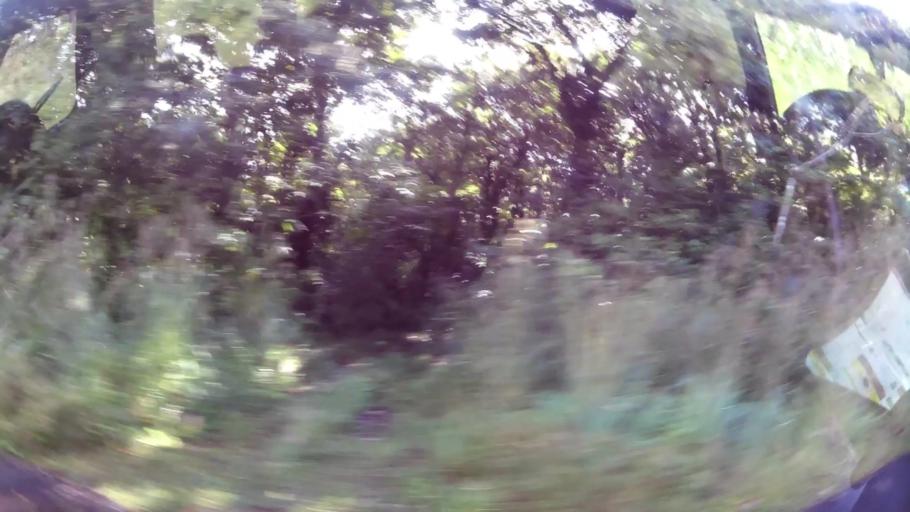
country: DM
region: Saint Paul
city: Pont Casse
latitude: 15.3803
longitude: -61.3407
